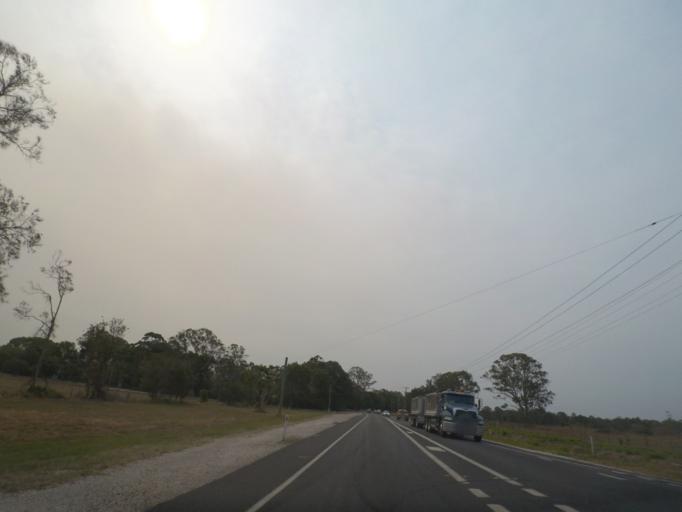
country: AU
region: New South Wales
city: Chinderah
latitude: -28.2519
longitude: 153.5584
